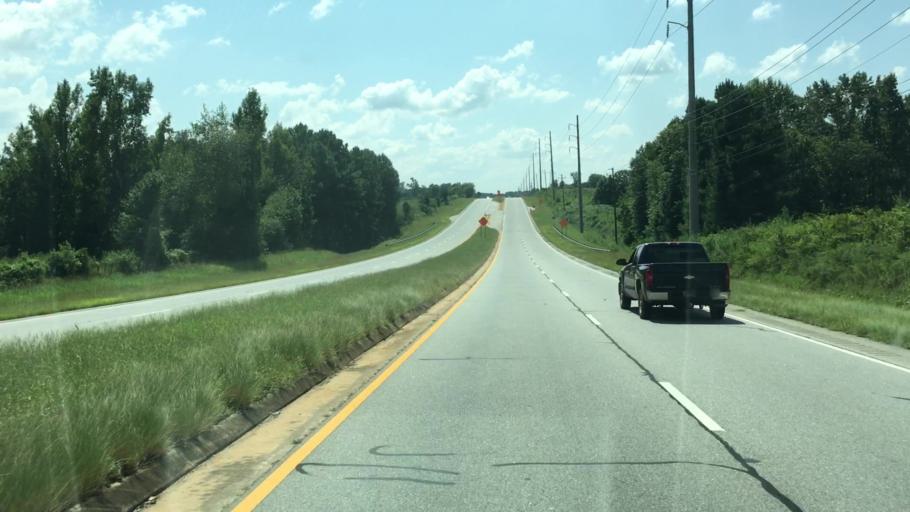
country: US
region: Georgia
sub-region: Morgan County
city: Madison
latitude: 33.5712
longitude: -83.4641
